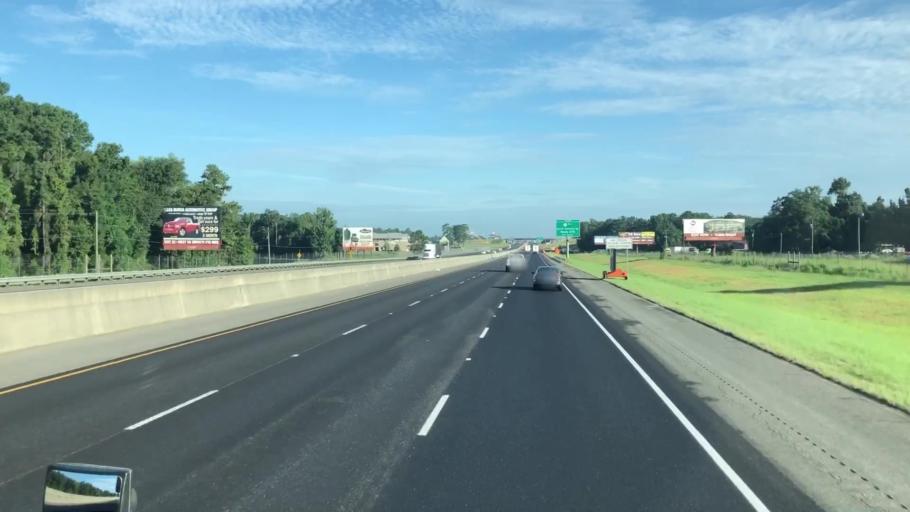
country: US
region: Georgia
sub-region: Lowndes County
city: Remerton
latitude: 30.8844
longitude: -83.3486
